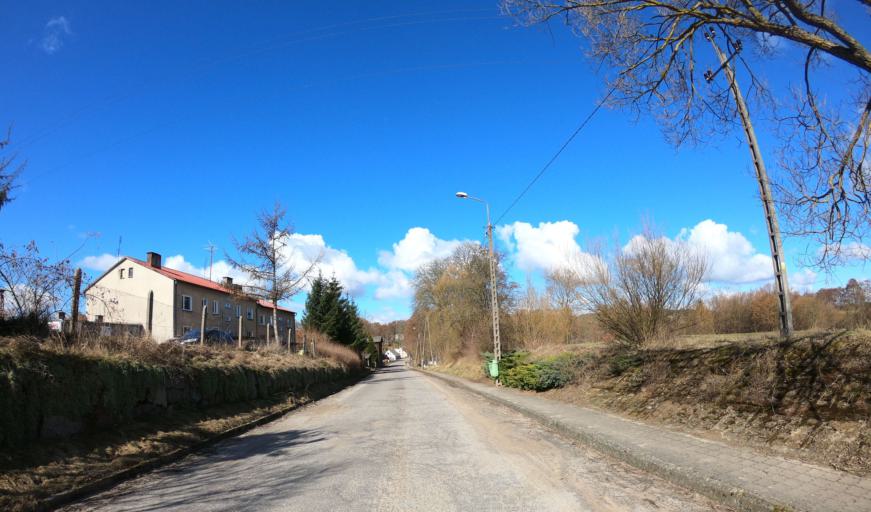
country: PL
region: West Pomeranian Voivodeship
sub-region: Powiat drawski
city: Zlocieniec
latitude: 53.4583
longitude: 15.9451
